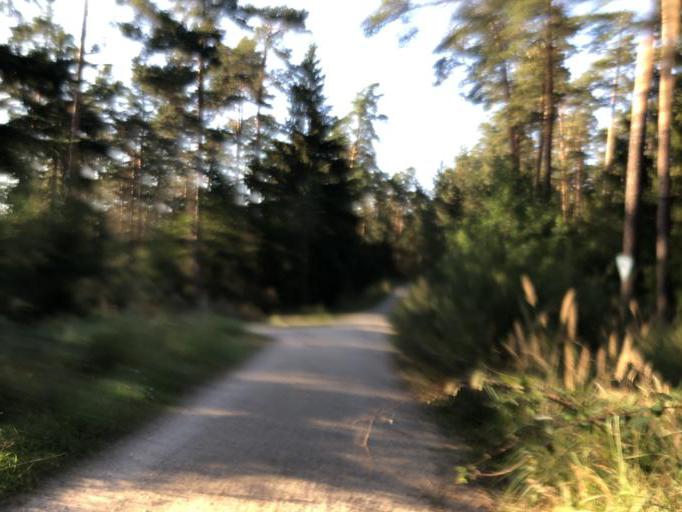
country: DE
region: Bavaria
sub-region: Regierungsbezirk Mittelfranken
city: Uttenreuth
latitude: 49.5630
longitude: 11.0850
